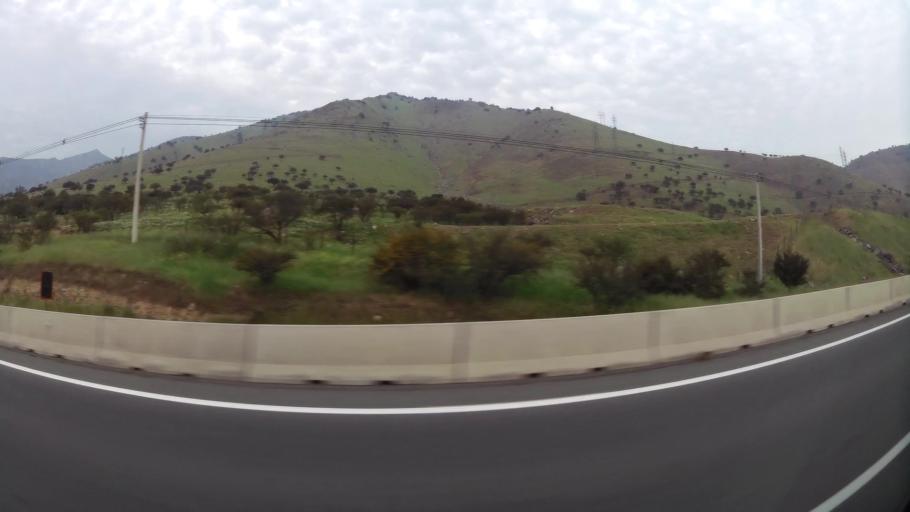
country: CL
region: Santiago Metropolitan
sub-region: Provincia de Chacabuco
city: Chicureo Abajo
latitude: -33.3598
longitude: -70.6168
